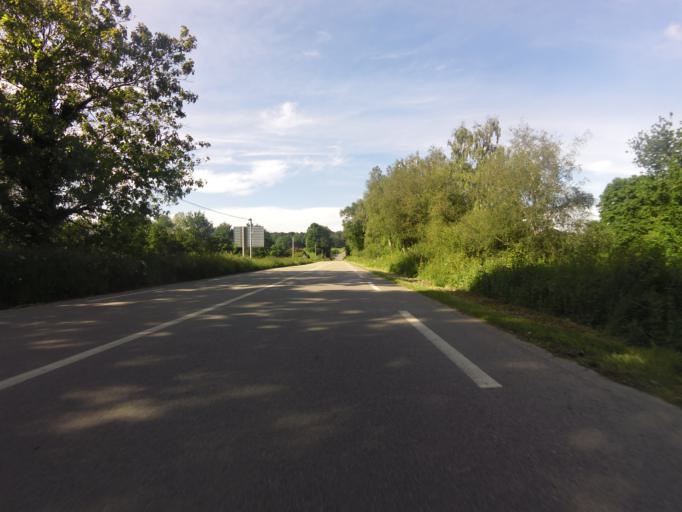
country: FR
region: Brittany
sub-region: Departement du Morbihan
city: Pluherlin
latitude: 47.7002
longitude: -2.3624
